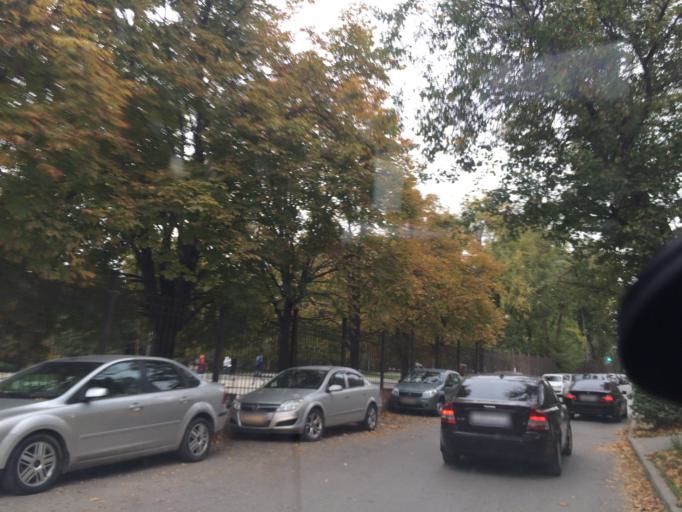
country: RU
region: Rostov
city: Rostov-na-Donu
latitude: 47.2065
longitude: 39.6236
